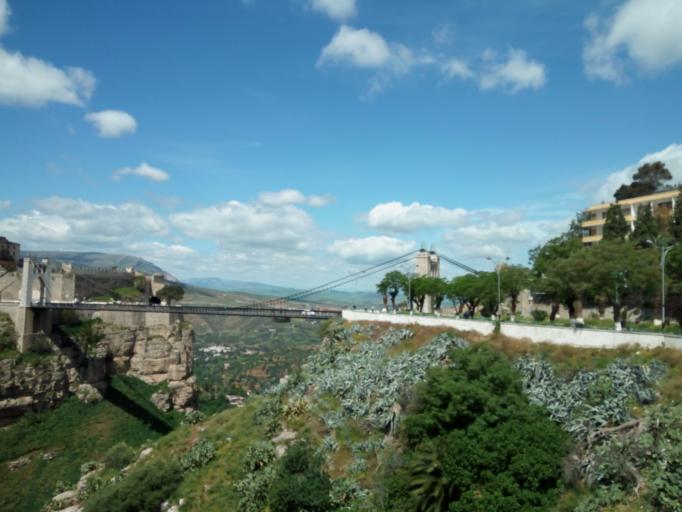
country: DZ
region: Constantine
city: Constantine
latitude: 36.3725
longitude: 6.6164
